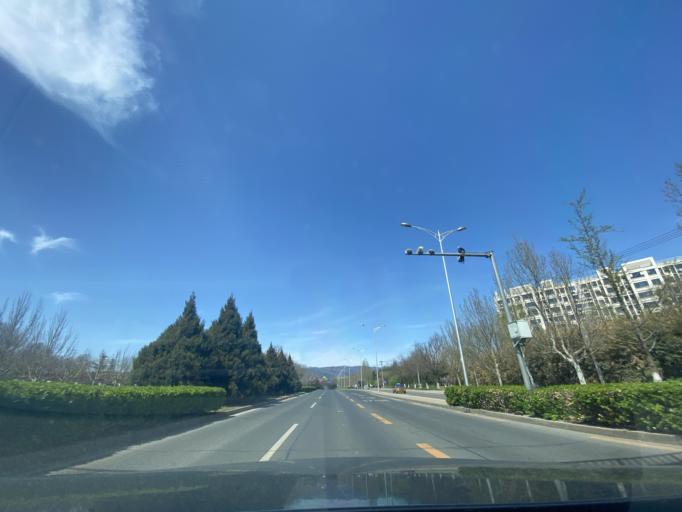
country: CN
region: Beijing
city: Sijiqing
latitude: 39.9353
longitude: 116.2441
